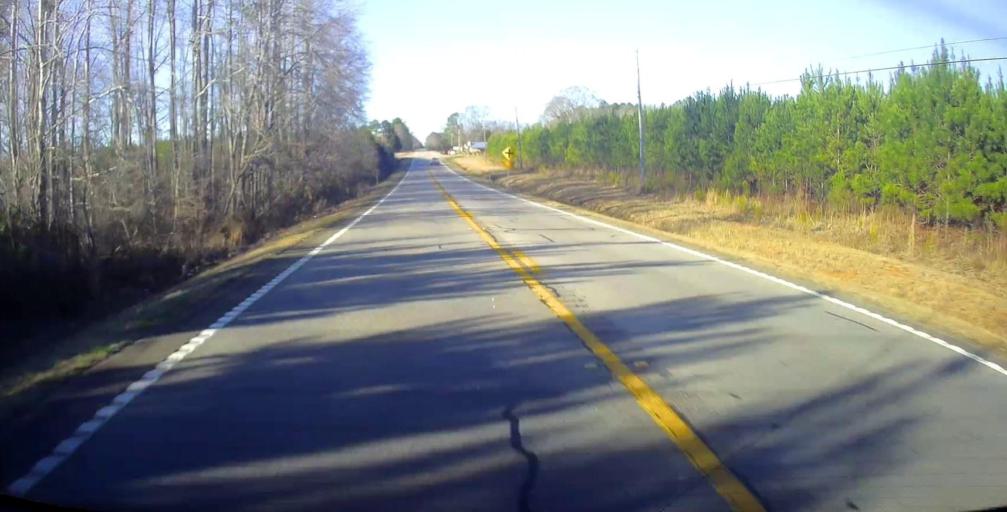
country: US
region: Georgia
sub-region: Meriwether County
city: Manchester
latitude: 32.8830
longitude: -84.5982
